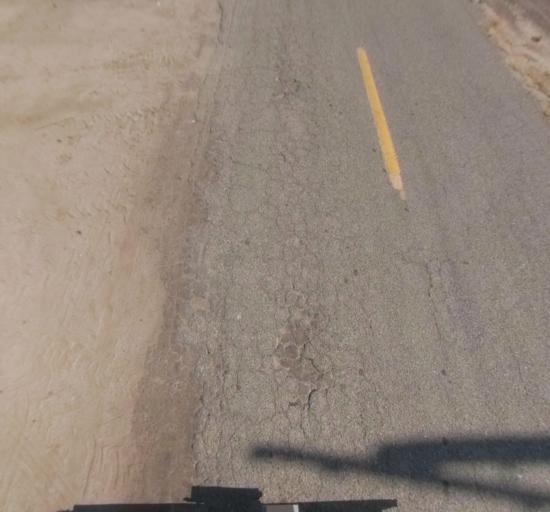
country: US
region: California
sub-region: Madera County
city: Parkwood
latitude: 36.8675
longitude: -120.1465
